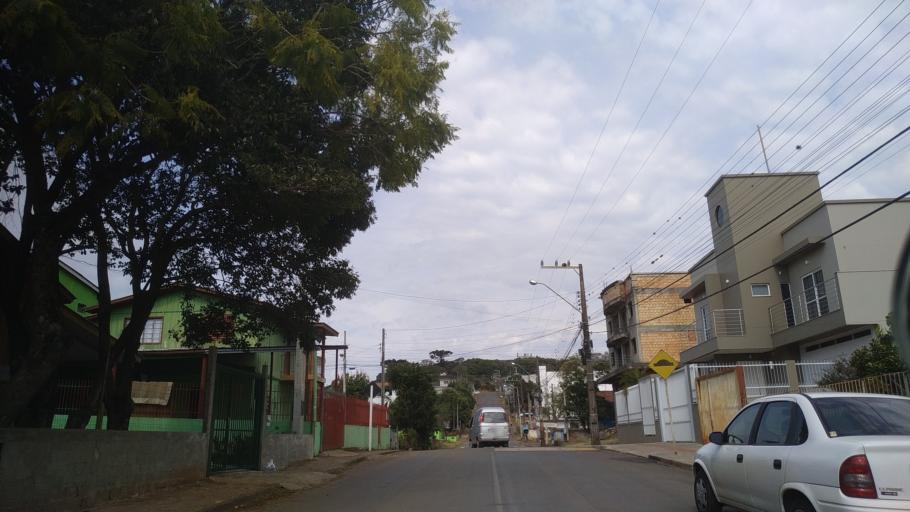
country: BR
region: Santa Catarina
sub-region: Chapeco
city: Chapeco
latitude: -27.1334
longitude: -52.6194
